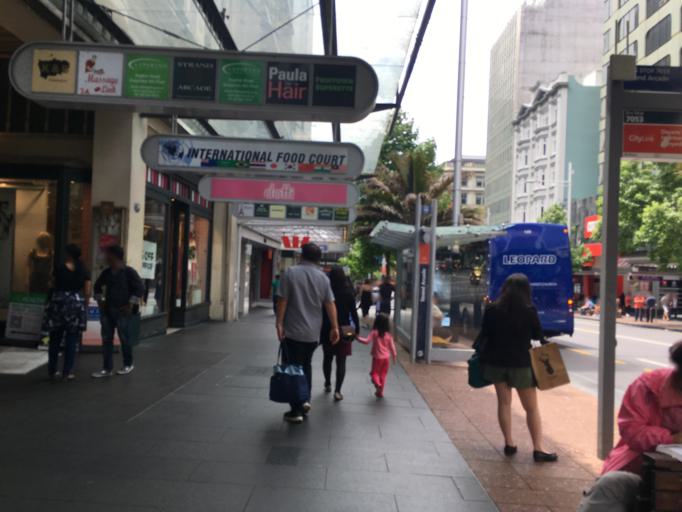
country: NZ
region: Auckland
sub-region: Auckland
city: Auckland
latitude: -36.8502
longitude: 174.7651
